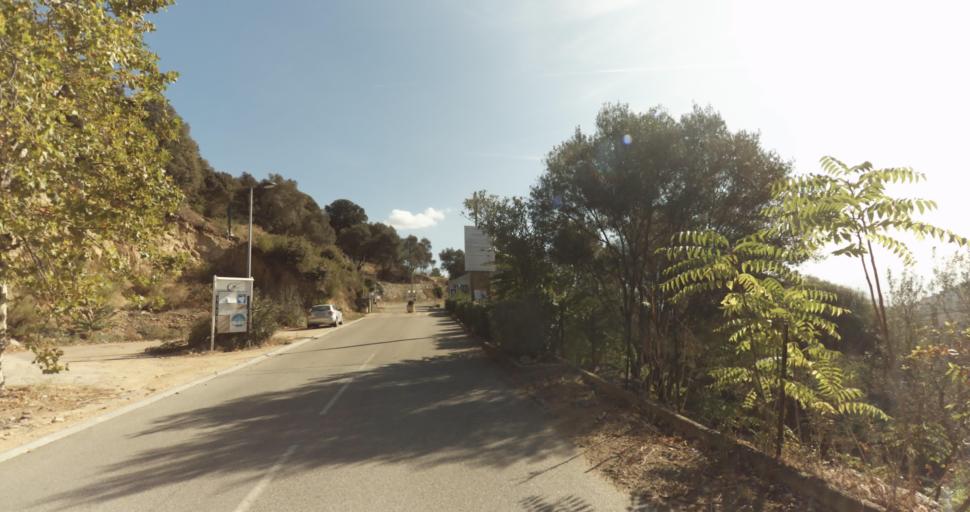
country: FR
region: Corsica
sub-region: Departement de la Corse-du-Sud
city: Ajaccio
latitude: 41.9336
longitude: 8.7096
